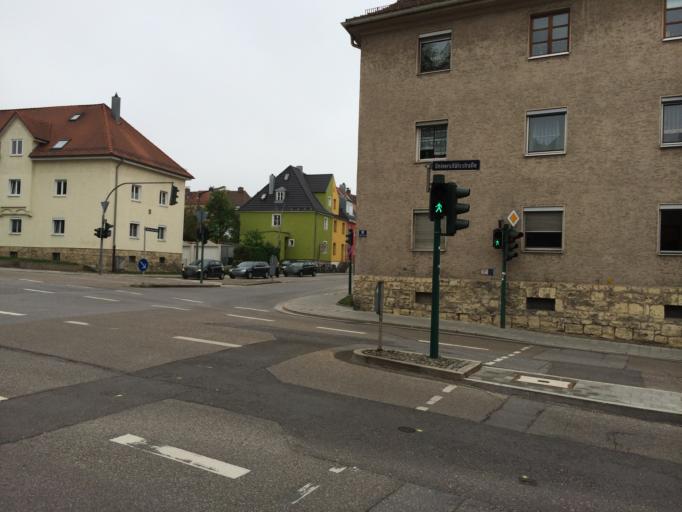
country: DE
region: Bavaria
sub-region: Upper Palatinate
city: Regensburg
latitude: 49.0071
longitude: 12.0930
